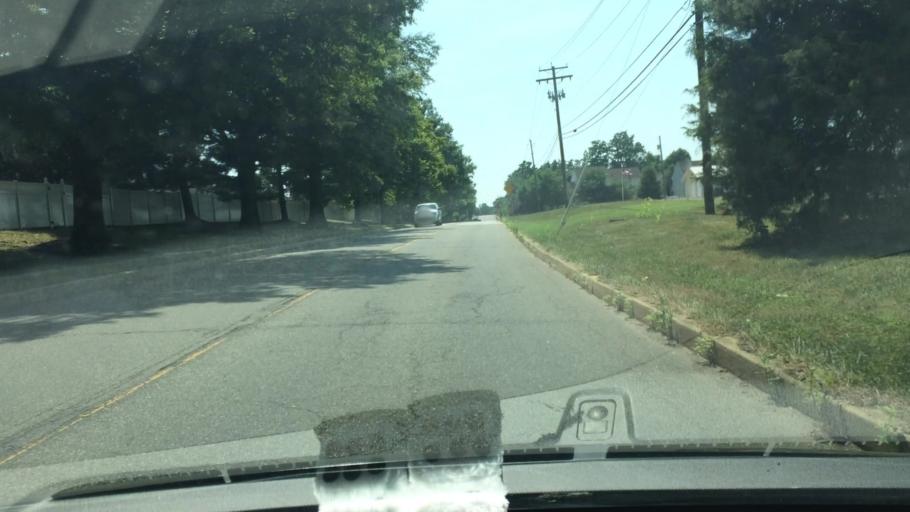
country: US
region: New Jersey
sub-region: Gloucester County
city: Beckett
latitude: 39.7547
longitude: -75.3614
